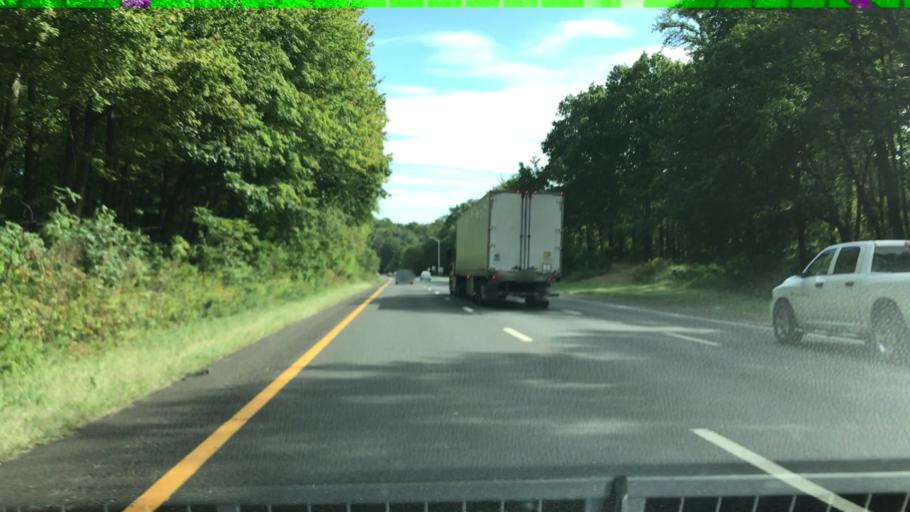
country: US
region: New Jersey
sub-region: Burlington County
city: Roebling
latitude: 40.0628
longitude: -74.8034
